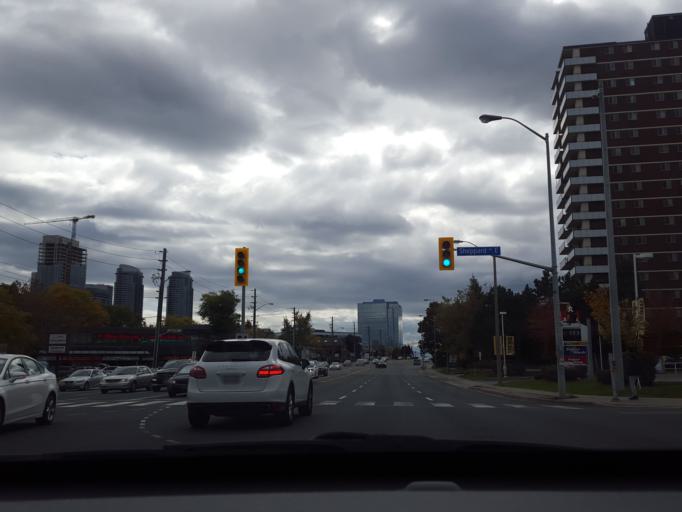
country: CA
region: Ontario
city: Scarborough
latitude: 43.7833
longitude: -79.2884
